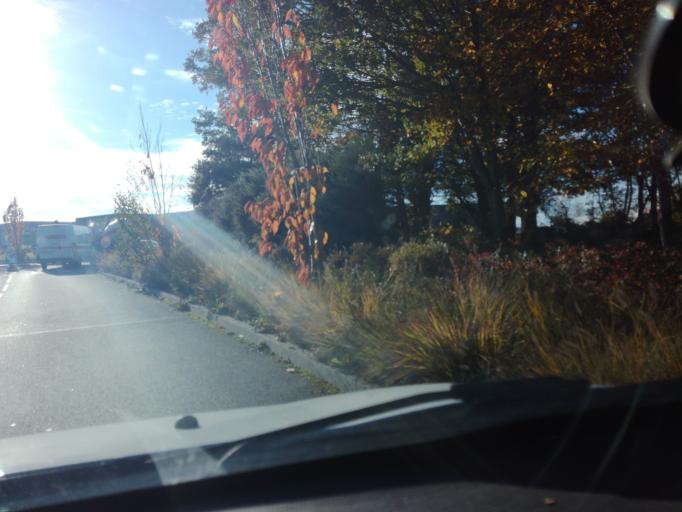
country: FR
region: Brittany
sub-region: Departement des Cotes-d'Armor
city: Lehon
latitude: 48.4699
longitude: -2.0509
